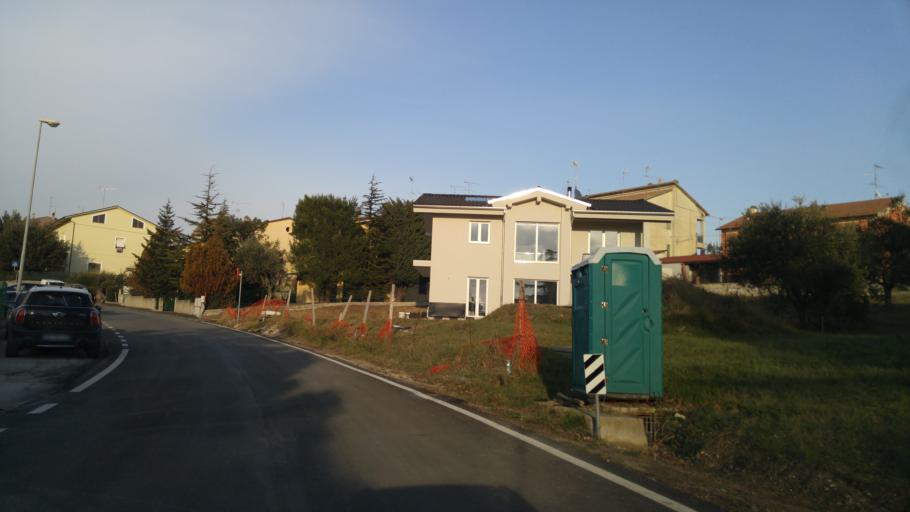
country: IT
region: The Marches
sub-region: Provincia di Pesaro e Urbino
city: Piagge
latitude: 43.7352
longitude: 12.9684
